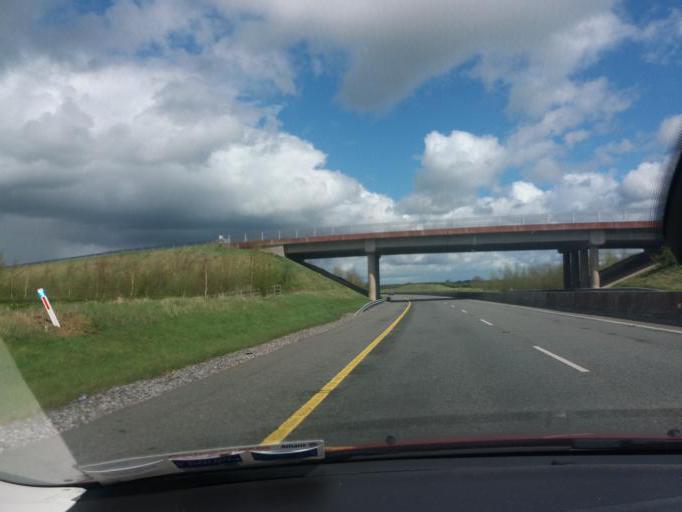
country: IE
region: Leinster
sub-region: Laois
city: Rathdowney
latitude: 52.8073
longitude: -7.4974
